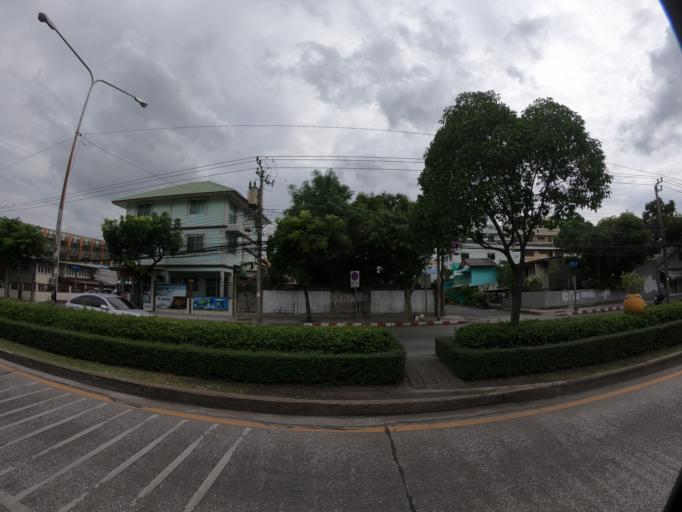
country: TH
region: Bangkok
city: Bang Kapi
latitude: 13.7736
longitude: 100.6463
